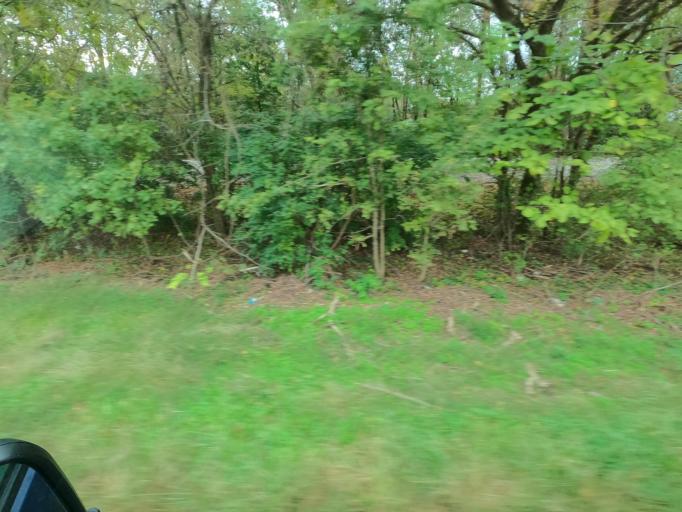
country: US
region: Tennessee
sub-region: Cheatham County
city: Pegram
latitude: 36.0960
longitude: -87.0439
